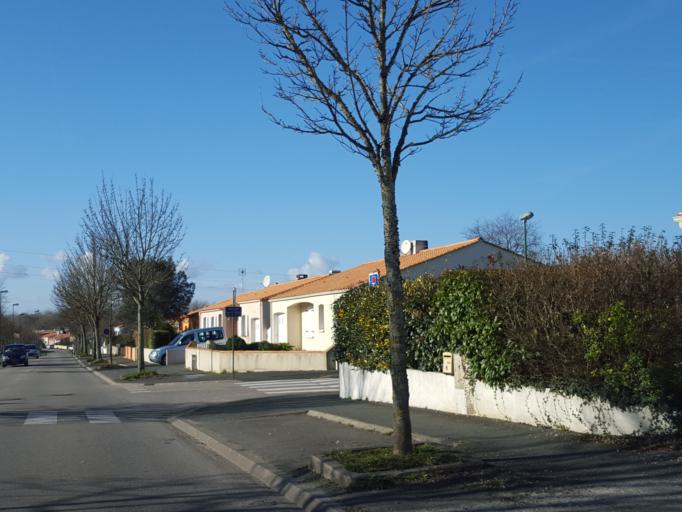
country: FR
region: Pays de la Loire
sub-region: Departement de la Vendee
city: La Roche-sur-Yon
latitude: 46.6605
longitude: -1.4518
